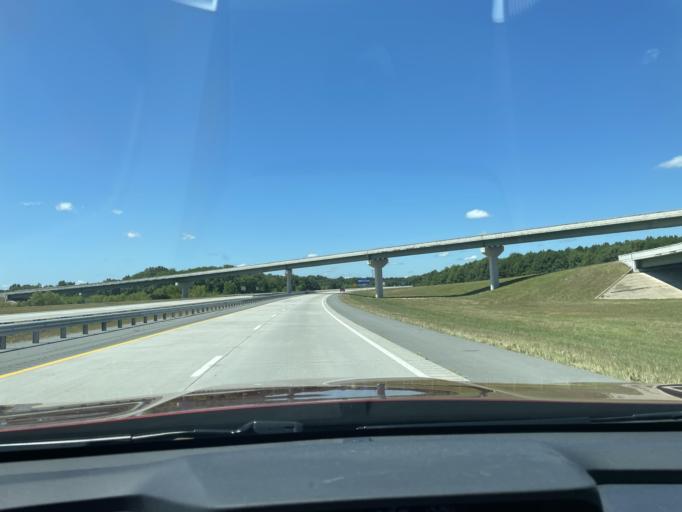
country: US
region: Arkansas
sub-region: Jefferson County
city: Pine Bluff
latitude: 34.1747
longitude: -91.9906
